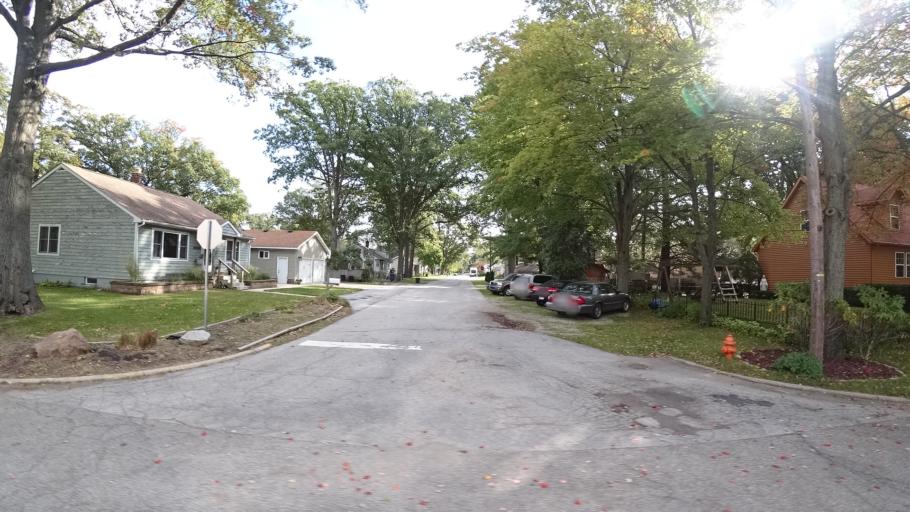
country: US
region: Indiana
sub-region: LaPorte County
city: Trail Creek
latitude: 41.7046
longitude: -86.8726
